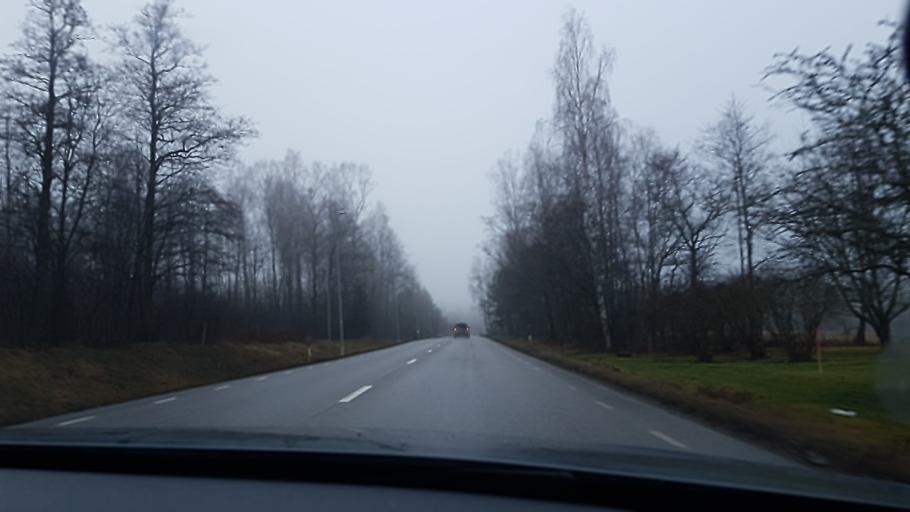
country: SE
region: Vaestra Goetaland
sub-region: Gullspangs Kommun
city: Gullspang
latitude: 58.9775
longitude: 14.0818
